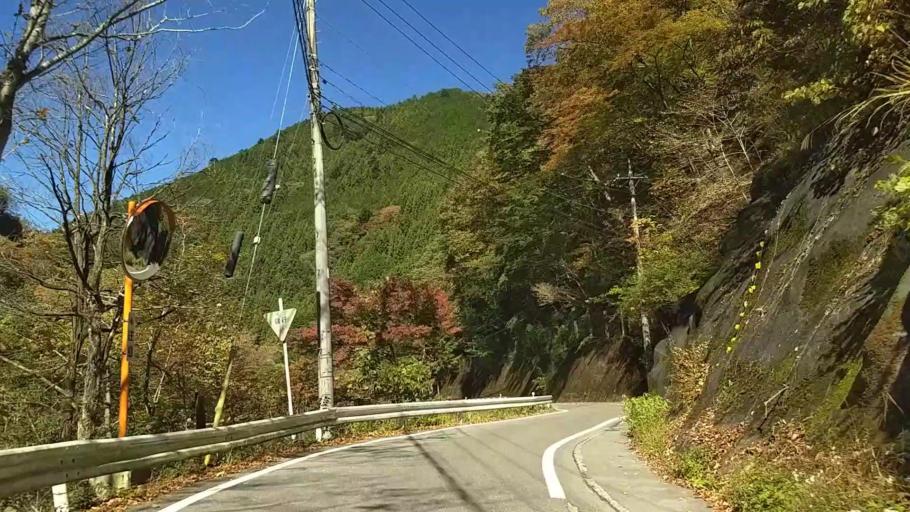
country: JP
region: Yamanashi
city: Uenohara
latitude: 35.6813
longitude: 139.0520
